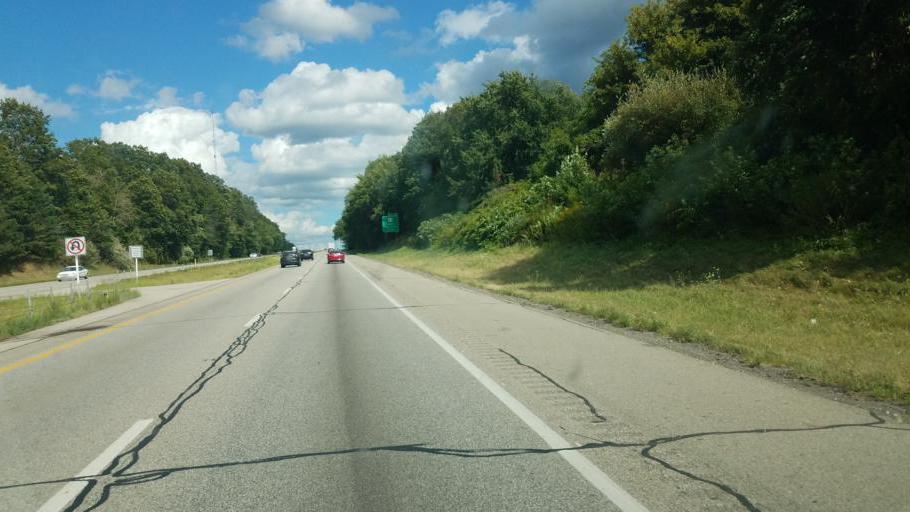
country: US
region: Ohio
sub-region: Portage County
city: Brimfield
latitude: 41.1065
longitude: -81.3625
